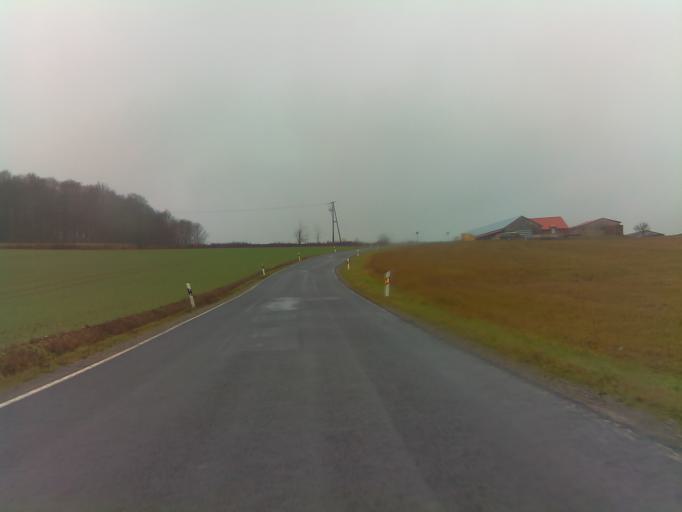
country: DE
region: Thuringia
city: Dingsleben
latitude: 50.4295
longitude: 10.6041
